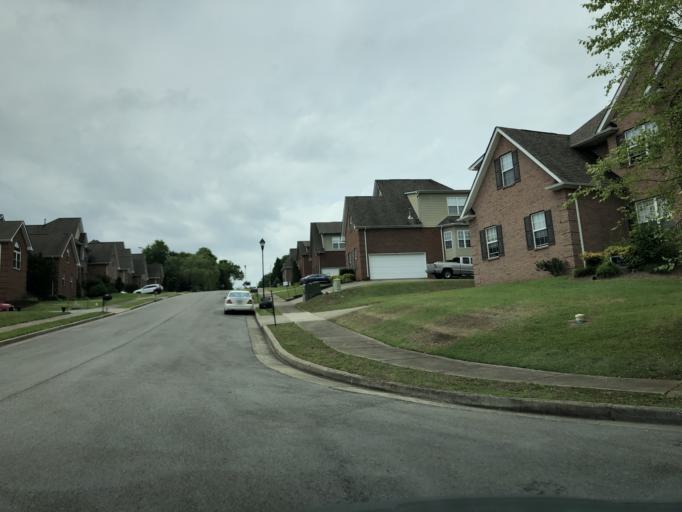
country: US
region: Tennessee
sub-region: Davidson County
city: Goodlettsville
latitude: 36.2817
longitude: -86.7421
